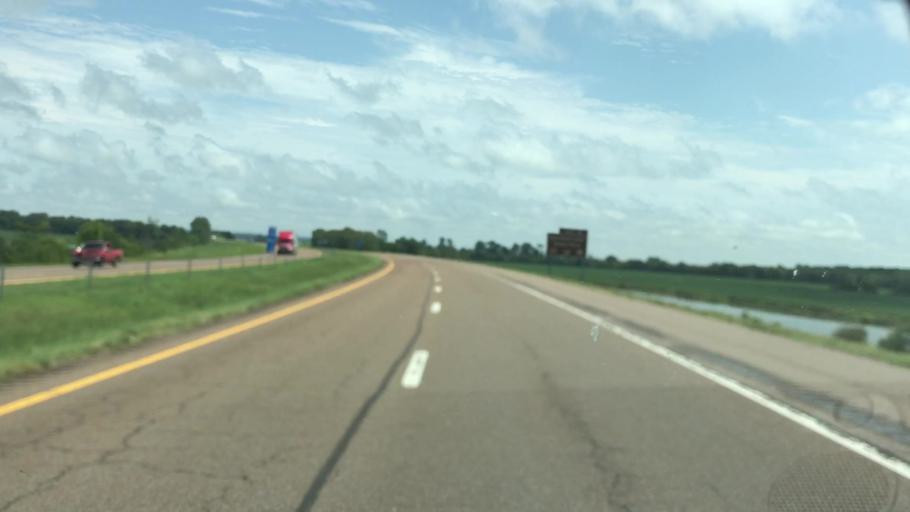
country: US
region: Missouri
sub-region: Pemiscot County
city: Caruthersville
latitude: 36.0964
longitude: -89.5997
